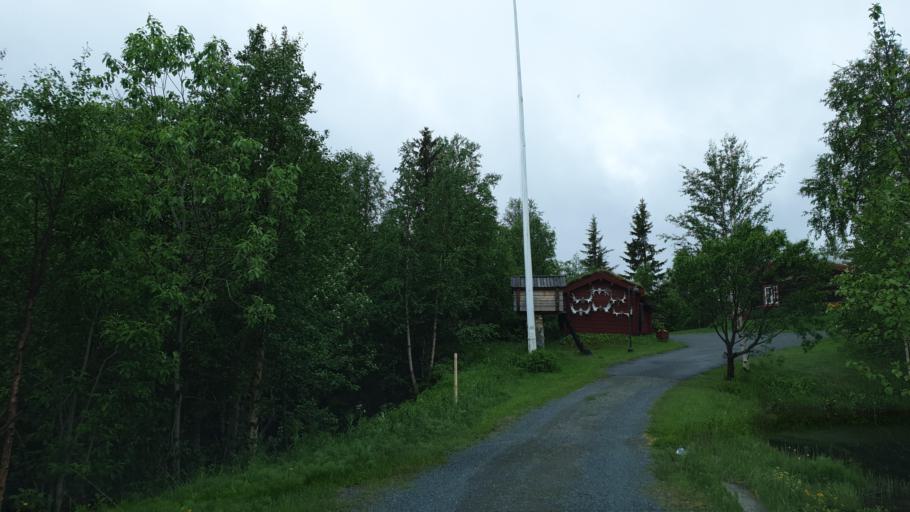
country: SE
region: Vaesterbotten
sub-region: Vilhelmina Kommun
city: Sjoberg
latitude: 65.2506
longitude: 15.5609
